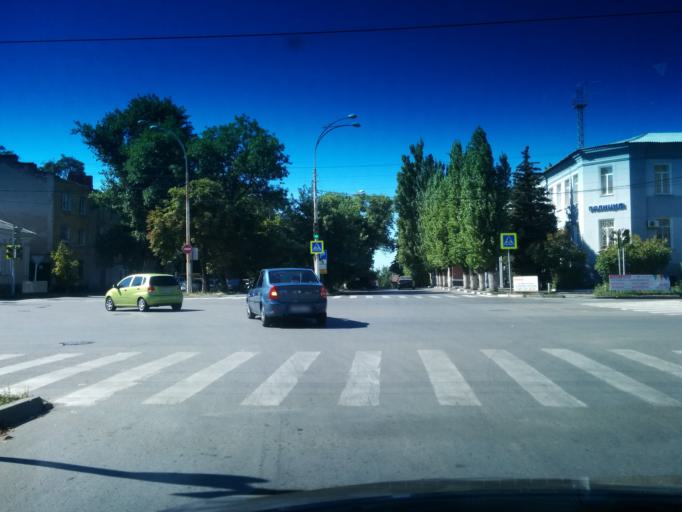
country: RU
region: Rostov
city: Shakhty
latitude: 47.7139
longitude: 40.2107
